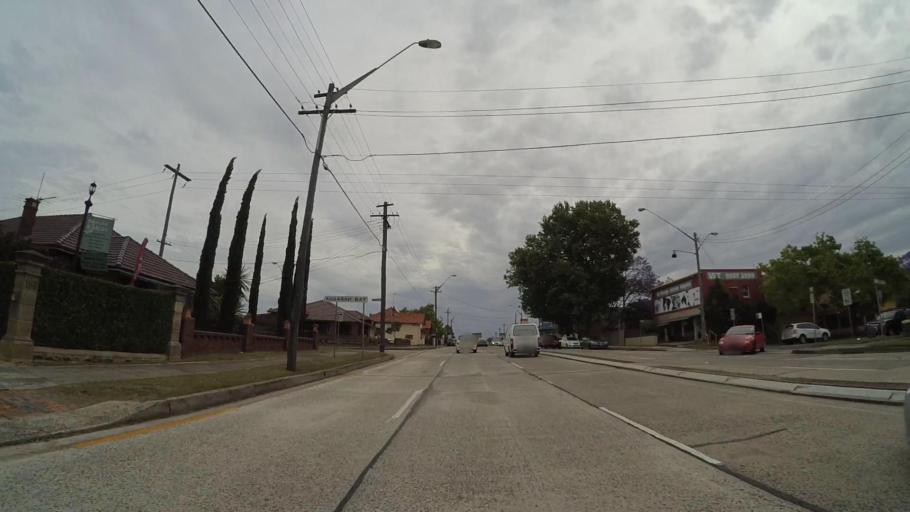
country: AU
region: New South Wales
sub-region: Kogarah
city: Kogarah Bay
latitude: -33.9771
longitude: 151.1246
